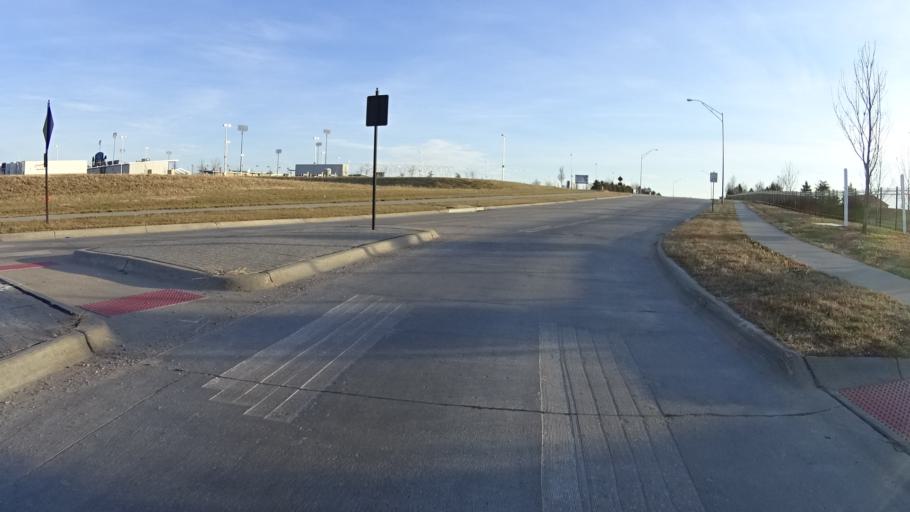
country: US
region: Nebraska
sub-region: Sarpy County
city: Chalco
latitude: 41.1542
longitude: -96.1102
